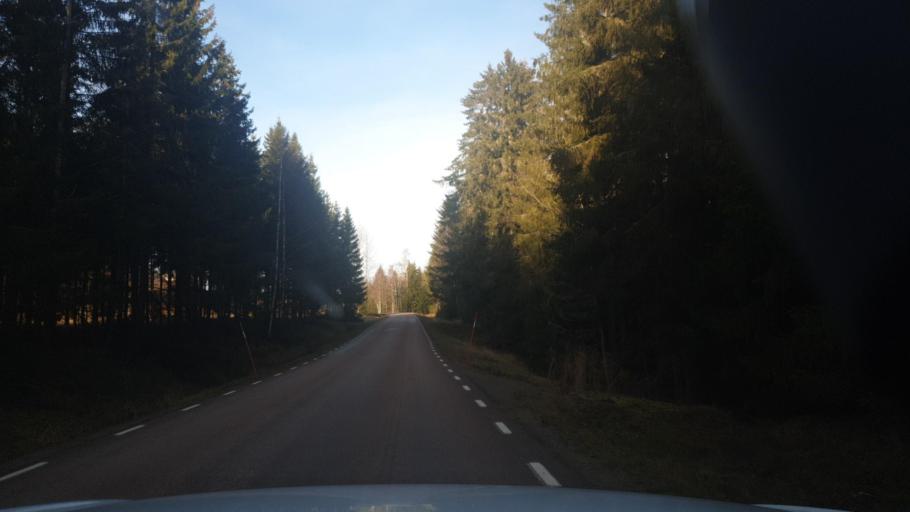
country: SE
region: Vaermland
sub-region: Grums Kommun
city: Slottsbron
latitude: 59.4570
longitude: 12.8817
